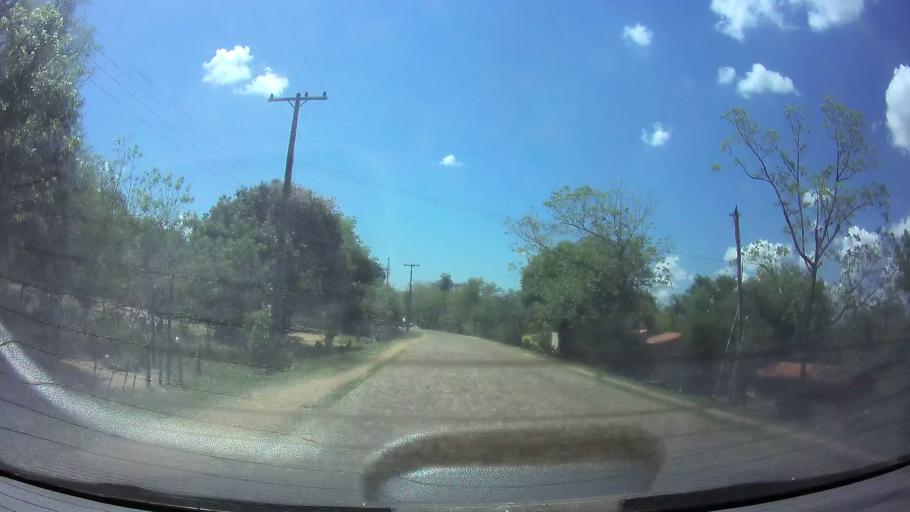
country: PY
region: Cordillera
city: Emboscada
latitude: -25.1159
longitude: -57.3095
